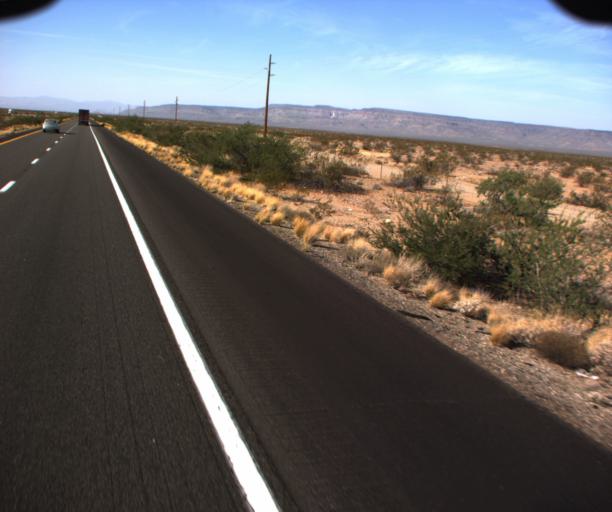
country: US
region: Arizona
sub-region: Mohave County
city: Kingman
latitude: 34.9920
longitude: -114.1386
